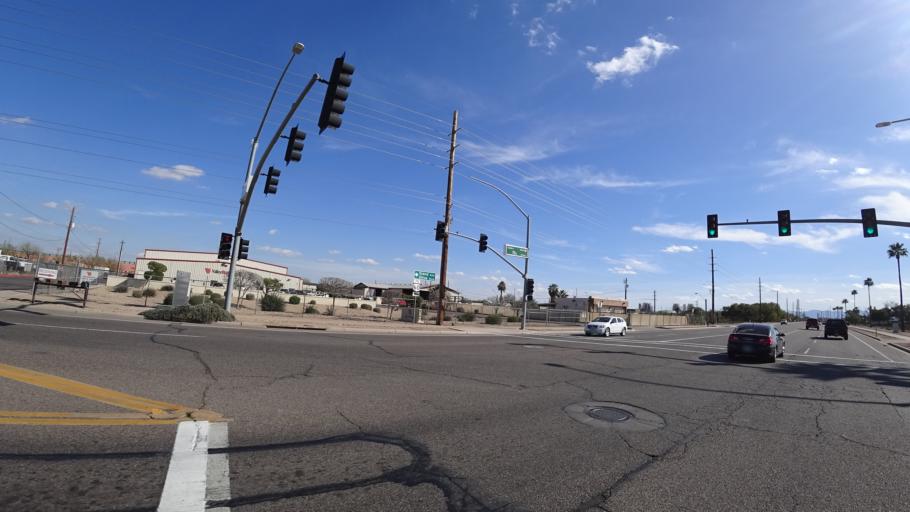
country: US
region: Arizona
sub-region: Maricopa County
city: Peoria
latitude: 33.5645
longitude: -112.2204
